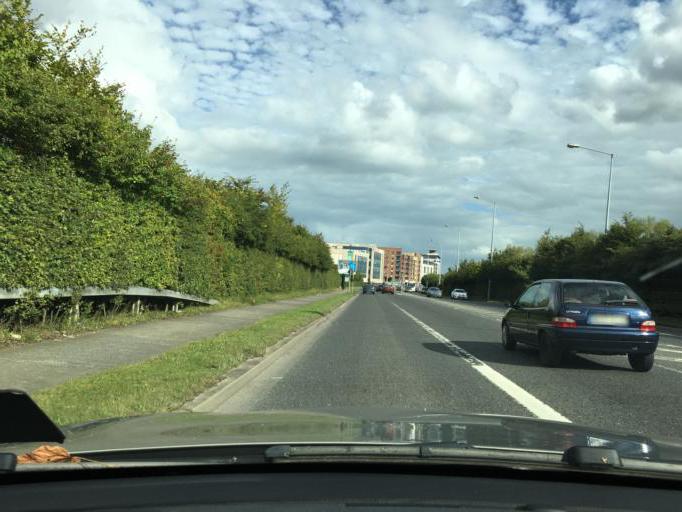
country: IE
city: Darndale
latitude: 53.4045
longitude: -6.1861
